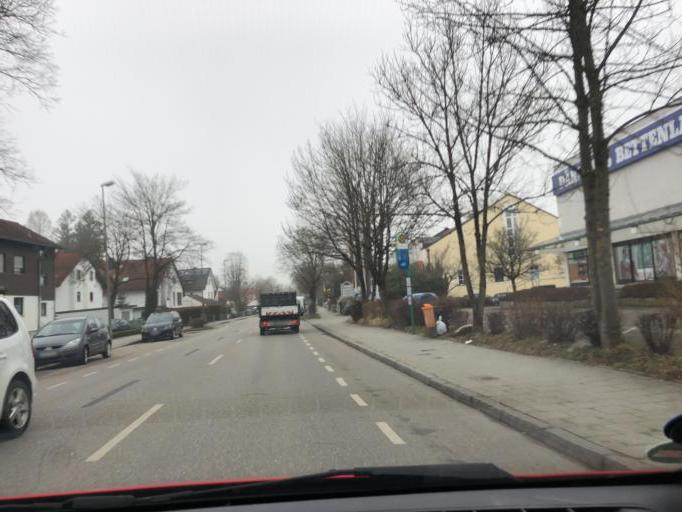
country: DE
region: Bavaria
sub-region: Upper Bavaria
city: Grobenzell
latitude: 48.1865
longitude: 11.3829
